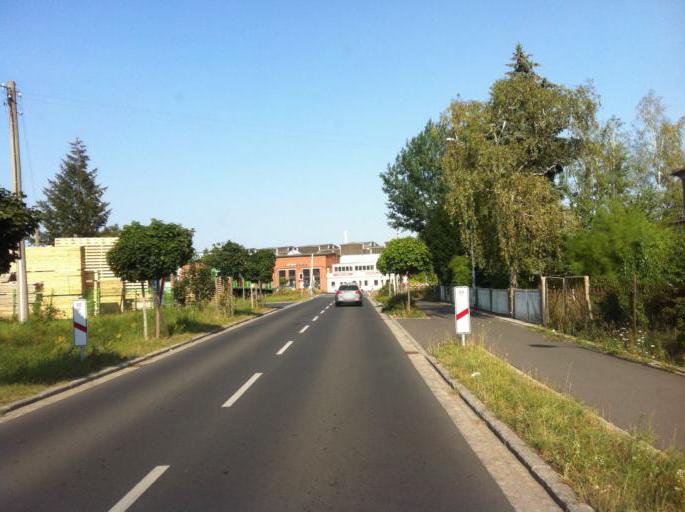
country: DE
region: Saxony
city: Grimma
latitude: 51.2248
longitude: 12.7129
